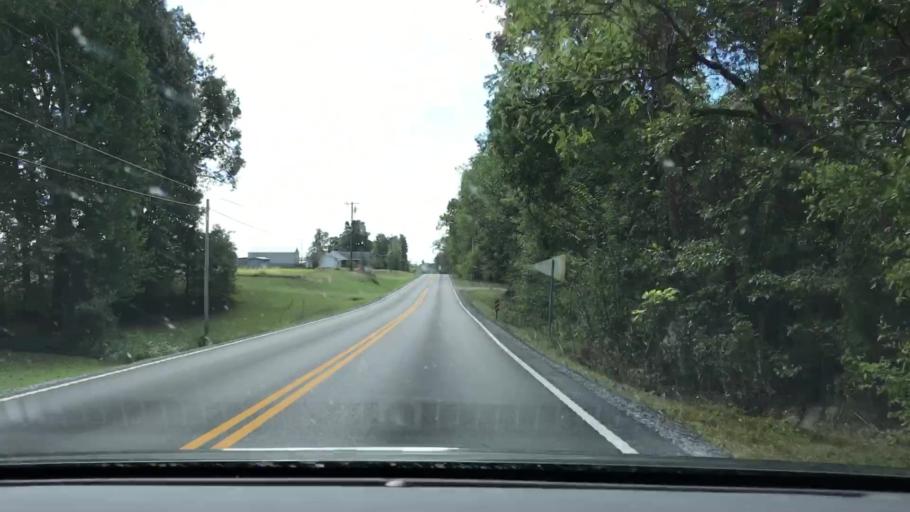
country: US
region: Kentucky
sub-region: Graves County
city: Mayfield
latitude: 36.7927
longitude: -88.5956
